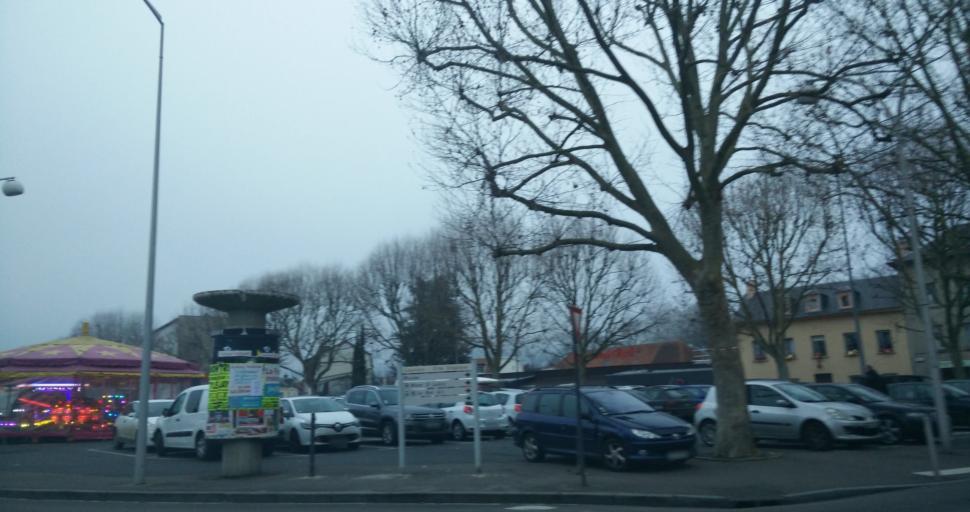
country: FR
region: Haute-Normandie
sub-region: Departement de l'Eure
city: Louviers
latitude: 49.2104
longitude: 1.1657
